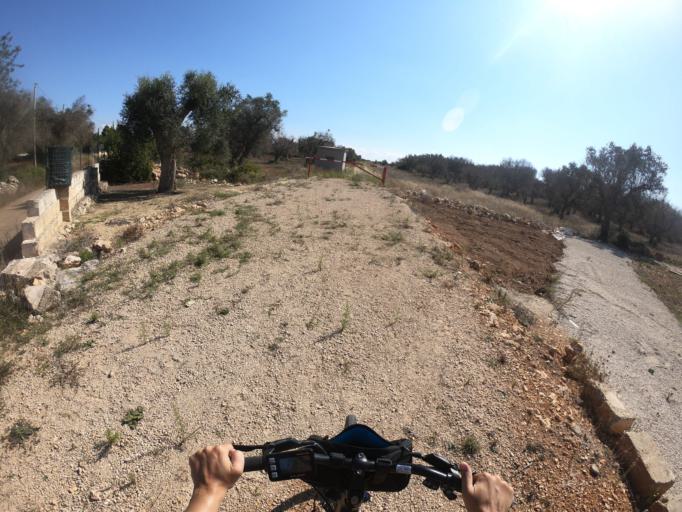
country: IT
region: Apulia
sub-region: Provincia di Lecce
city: Galatone
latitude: 40.1319
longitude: 18.0700
